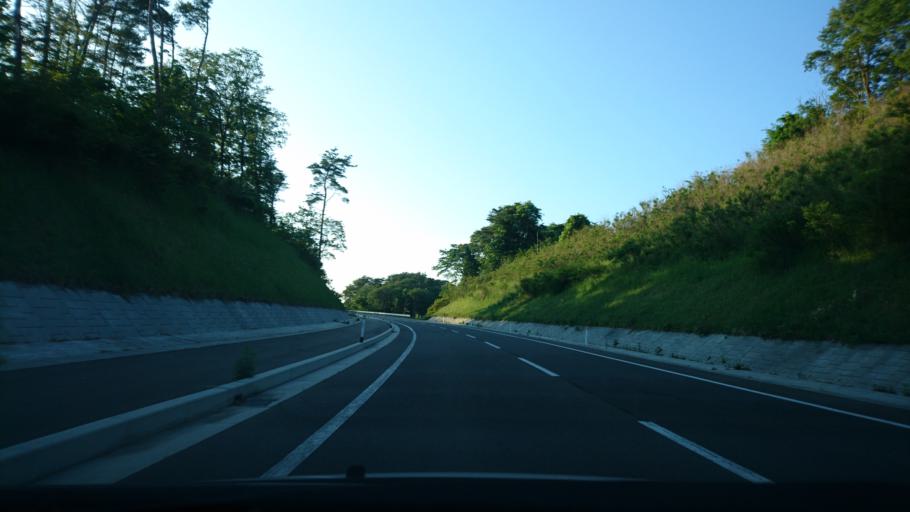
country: JP
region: Iwate
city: Ichinoseki
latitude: 38.8764
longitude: 141.1607
